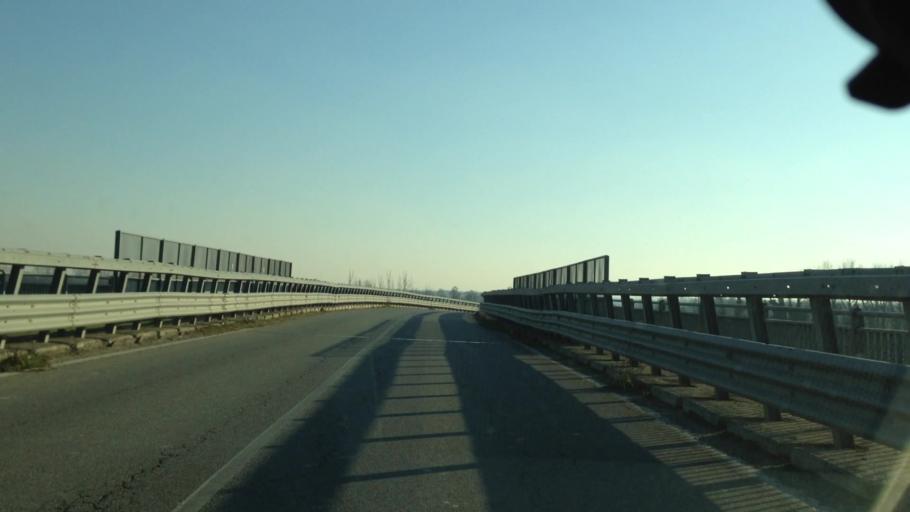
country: IT
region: Piedmont
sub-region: Provincia di Alessandria
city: Felizzano
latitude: 44.8977
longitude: 8.4502
